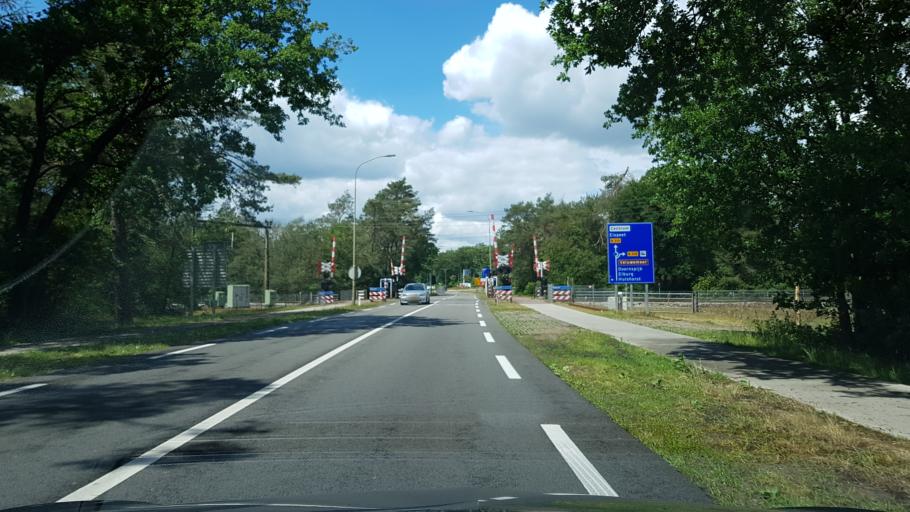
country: NL
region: Gelderland
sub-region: Gemeente Nunspeet
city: Nunspeet
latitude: 52.3768
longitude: 5.8156
